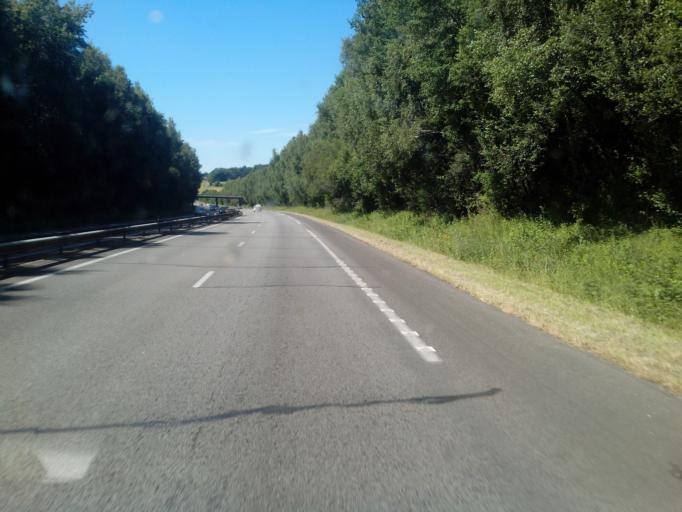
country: FR
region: Pays de la Loire
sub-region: Departement de la Loire-Atlantique
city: Treillieres
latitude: 47.3192
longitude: -1.6435
